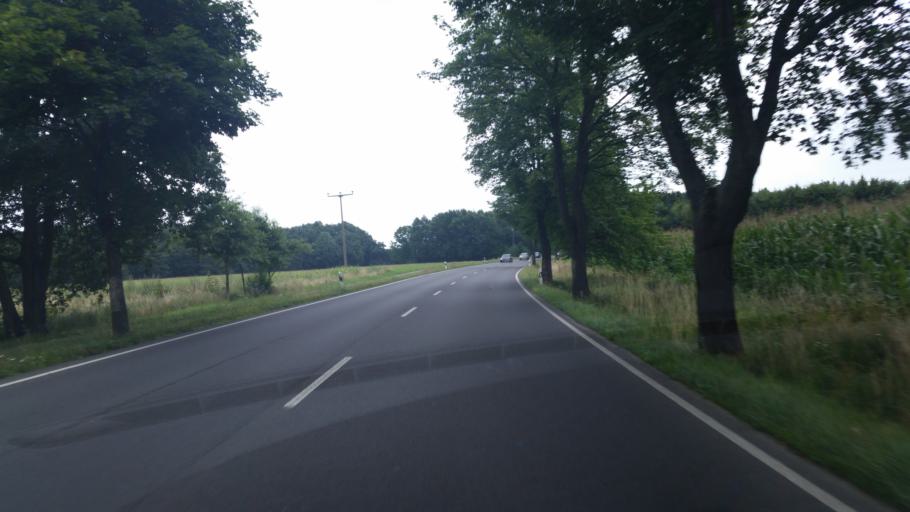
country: DE
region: Brandenburg
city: Senftenberg
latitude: 51.5103
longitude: 14.0591
